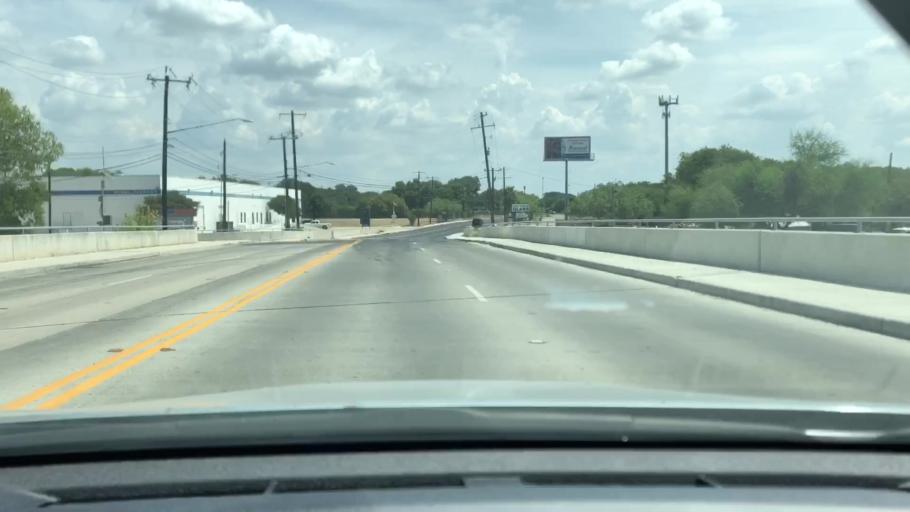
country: US
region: Texas
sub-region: Bexar County
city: Terrell Hills
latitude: 29.4849
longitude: -98.4160
